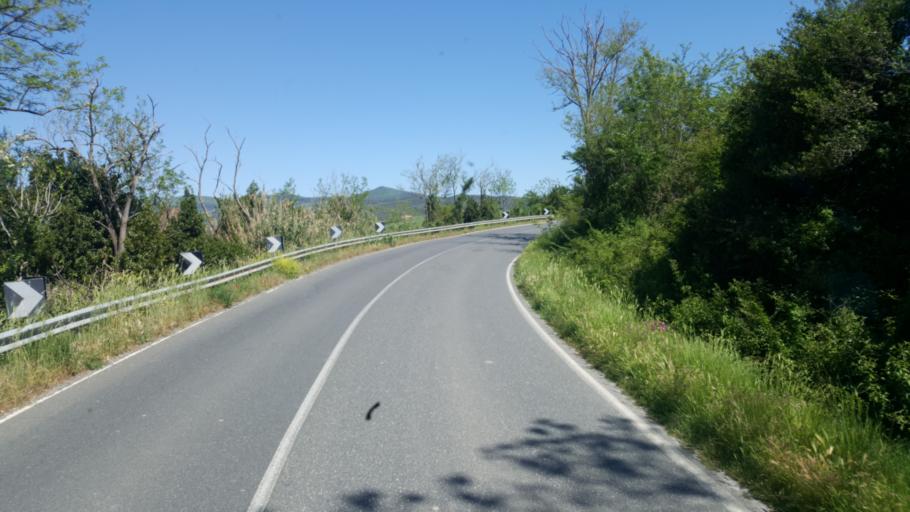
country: IT
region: Tuscany
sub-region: Provincia di Livorno
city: Rosignano Marittimo
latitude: 43.3956
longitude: 10.4974
